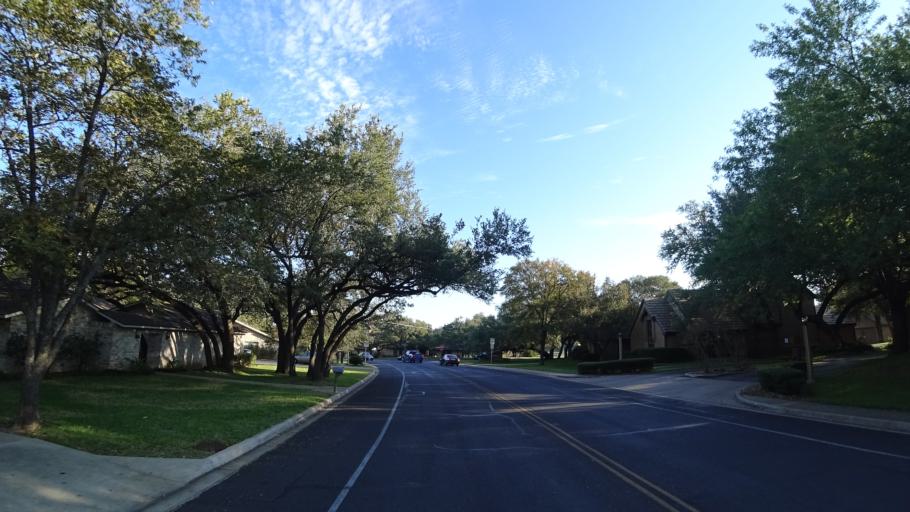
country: US
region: Texas
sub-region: Williamson County
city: Anderson Mill
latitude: 30.4427
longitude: -97.8062
